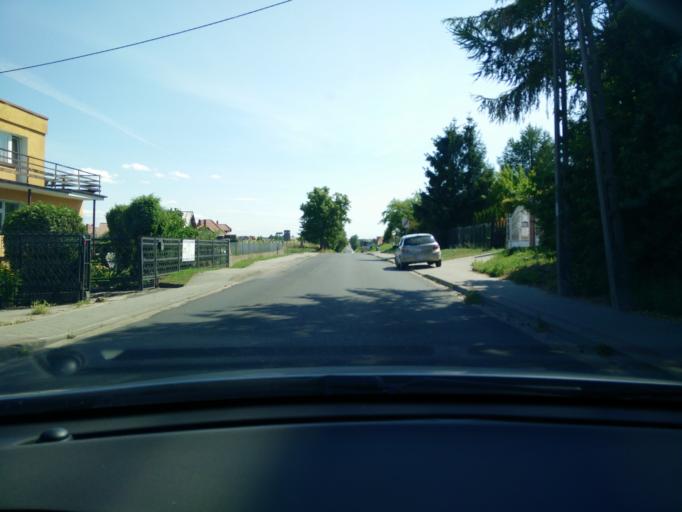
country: PL
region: Pomeranian Voivodeship
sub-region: Powiat pucki
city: Mosty
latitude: 54.6292
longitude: 18.4968
